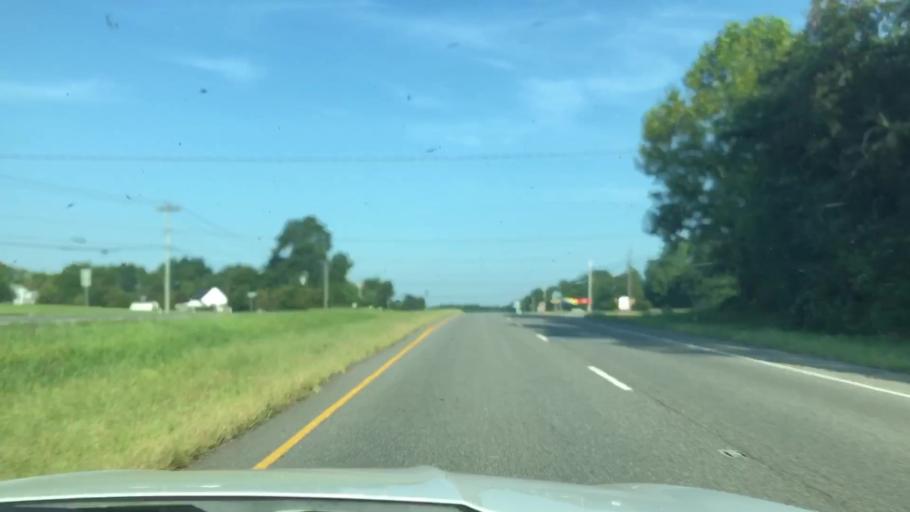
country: US
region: Virginia
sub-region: Essex County
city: Tappahannock
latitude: 37.8577
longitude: -76.8207
